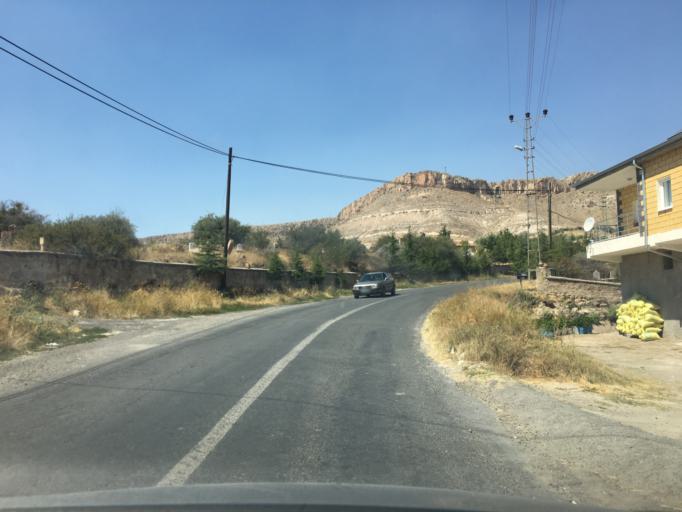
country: TR
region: Nevsehir
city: Urgub
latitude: 38.4690
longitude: 34.9524
